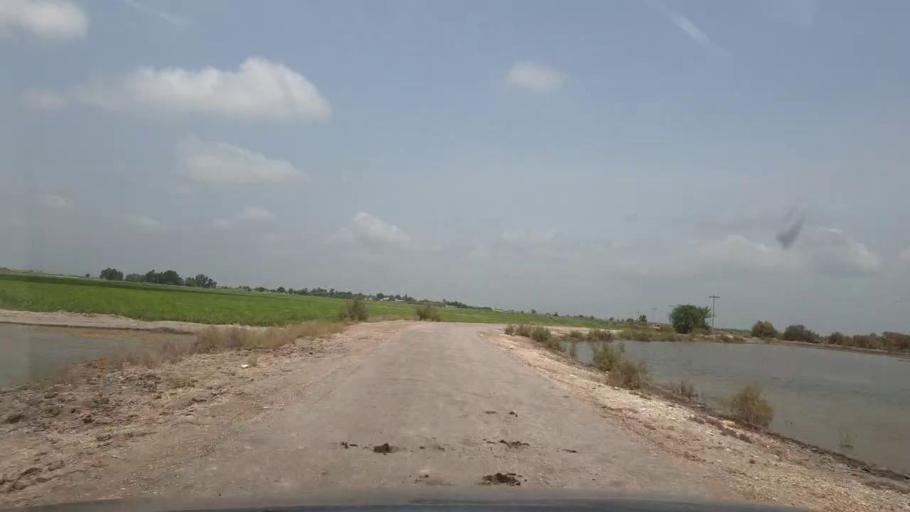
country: PK
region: Sindh
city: Ratodero
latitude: 27.9045
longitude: 68.3142
